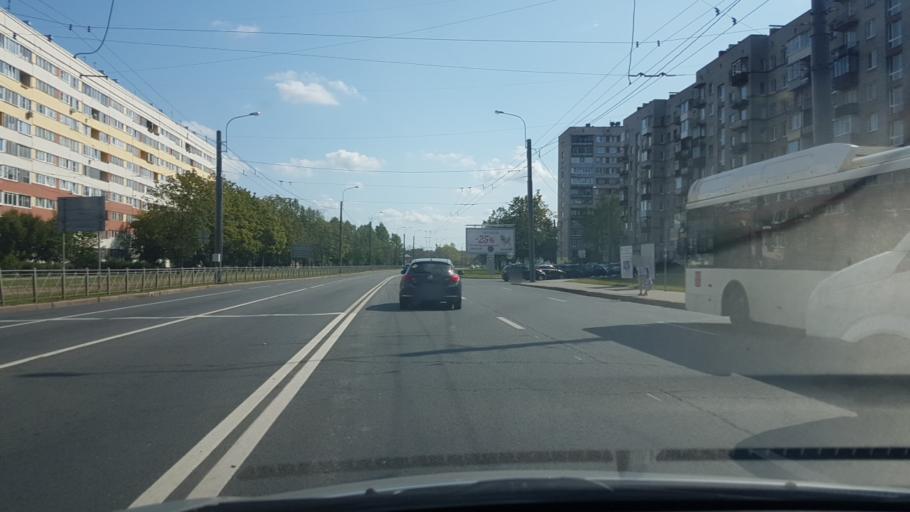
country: RU
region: St.-Petersburg
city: Sosnovaya Polyana
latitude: 59.8354
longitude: 30.1475
